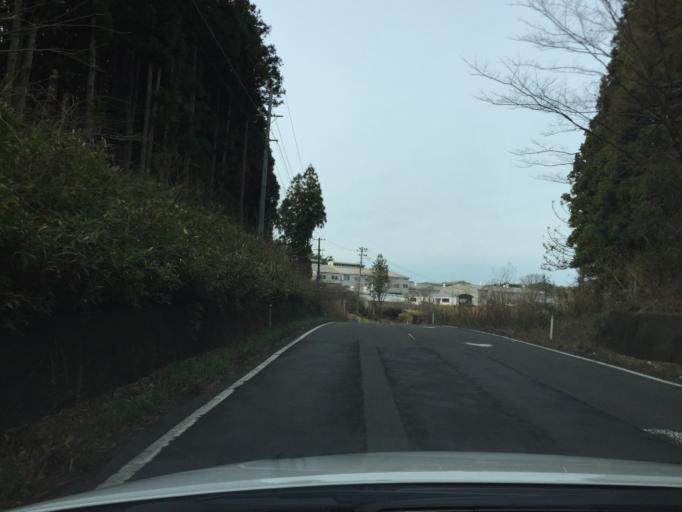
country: JP
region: Fukushima
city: Ishikawa
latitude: 37.2225
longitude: 140.6296
